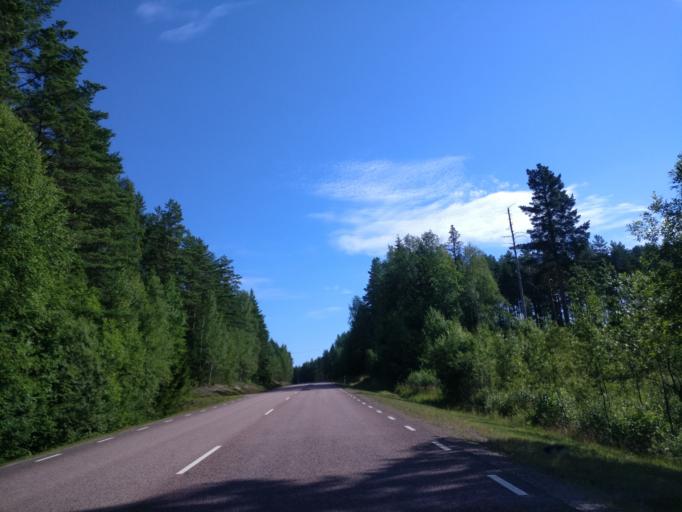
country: SE
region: Vaermland
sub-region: Hagfors Kommun
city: Hagfors
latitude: 60.0586
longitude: 13.7102
